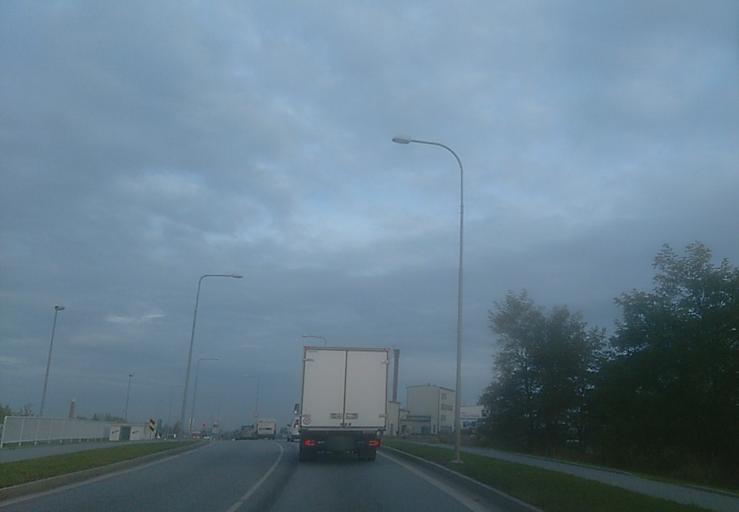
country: CZ
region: Jihocesky
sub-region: Okres Ceske Budejovice
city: Ceske Budejovice
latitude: 48.9801
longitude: 14.4901
